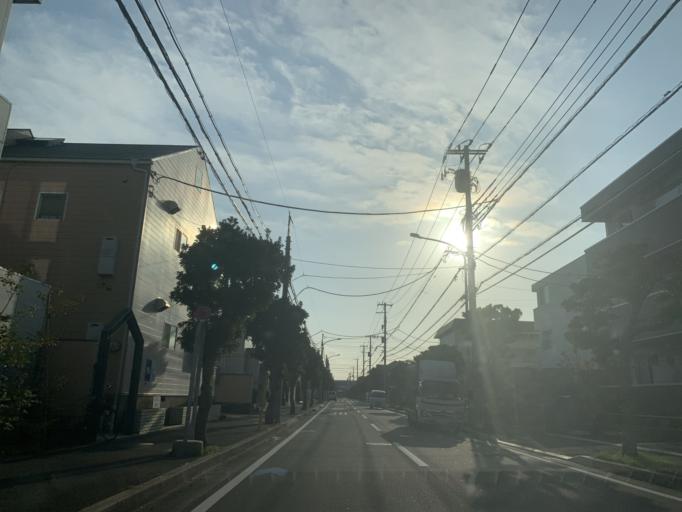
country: JP
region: Tokyo
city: Urayasu
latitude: 35.6413
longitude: 139.9068
